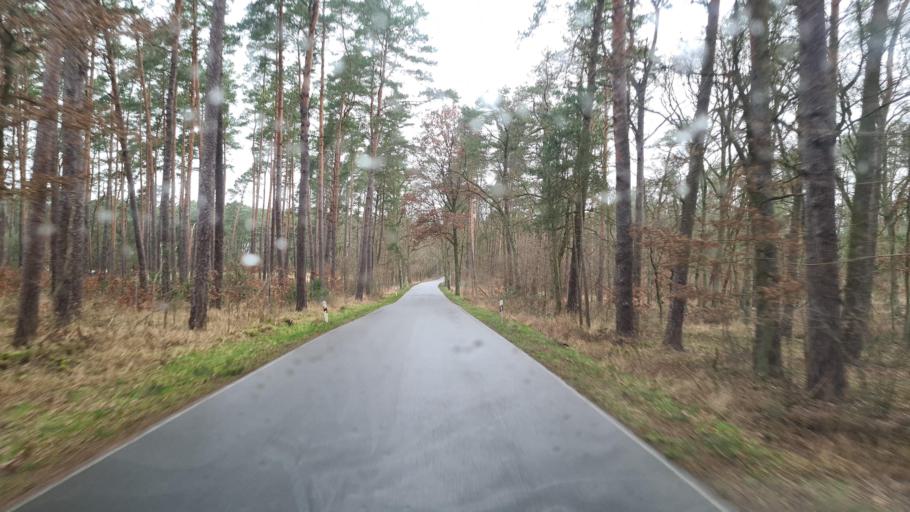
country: DE
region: Brandenburg
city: Gransee
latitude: 52.8864
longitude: 13.2059
